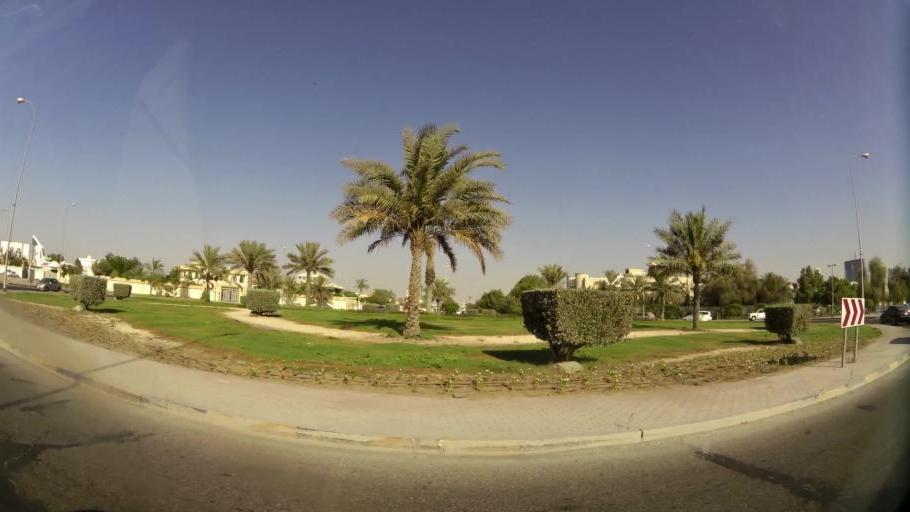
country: AE
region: Ajman
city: Ajman
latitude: 25.4056
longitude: 55.4719
